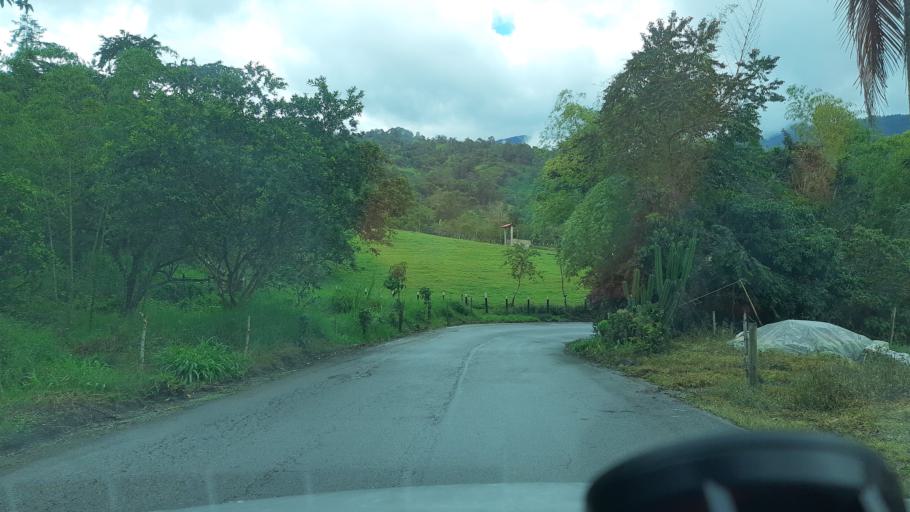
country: CO
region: Boyaca
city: Chinavita
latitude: 5.1413
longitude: -73.3640
